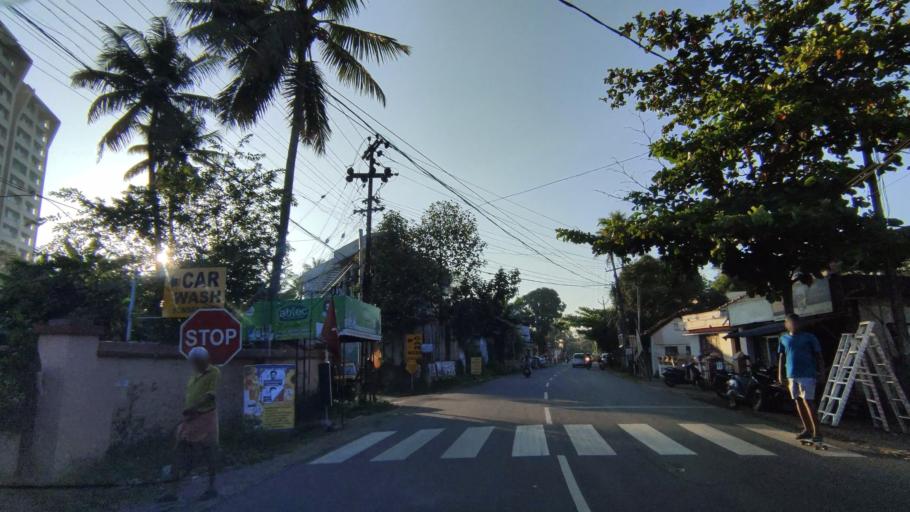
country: IN
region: Kerala
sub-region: Kottayam
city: Kottayam
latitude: 9.6081
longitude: 76.5105
